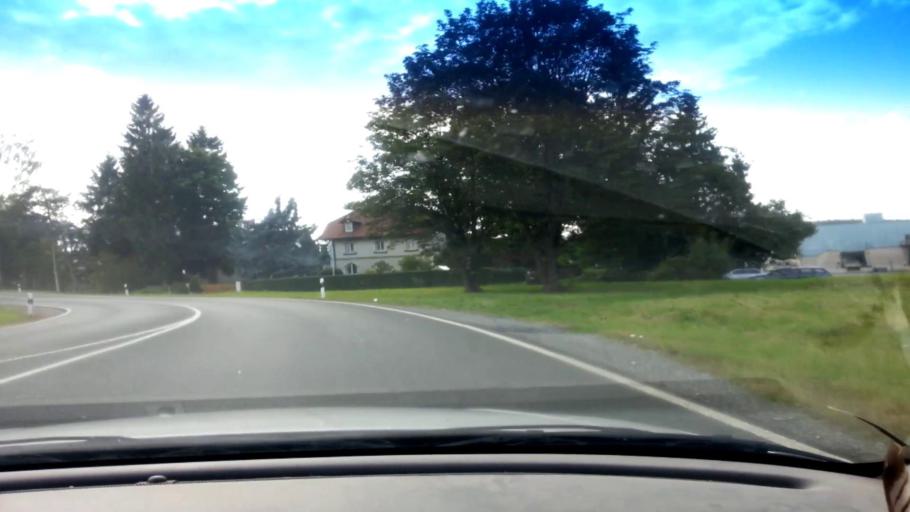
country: DE
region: Bavaria
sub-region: Upper Franconia
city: Marktredwitz
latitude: 50.0163
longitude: 12.1017
